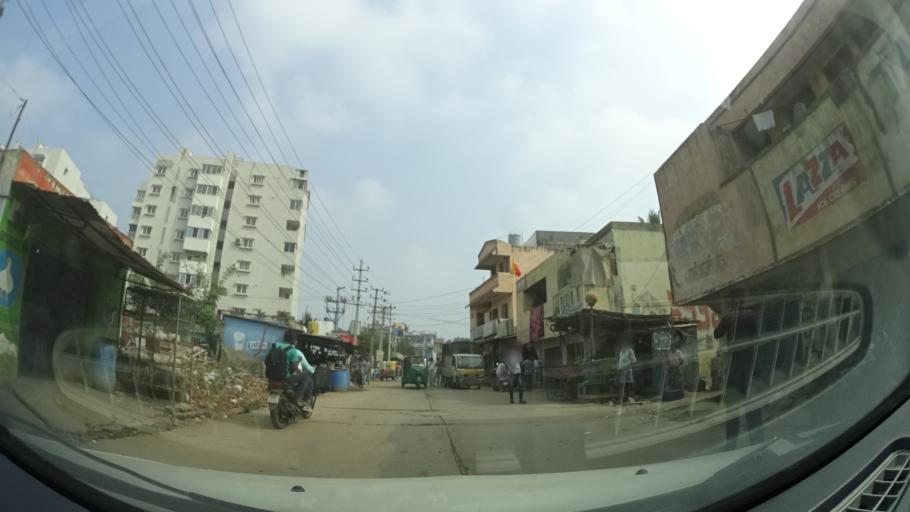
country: IN
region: Karnataka
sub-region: Bangalore Urban
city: Anekal
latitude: 12.8344
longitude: 77.6562
